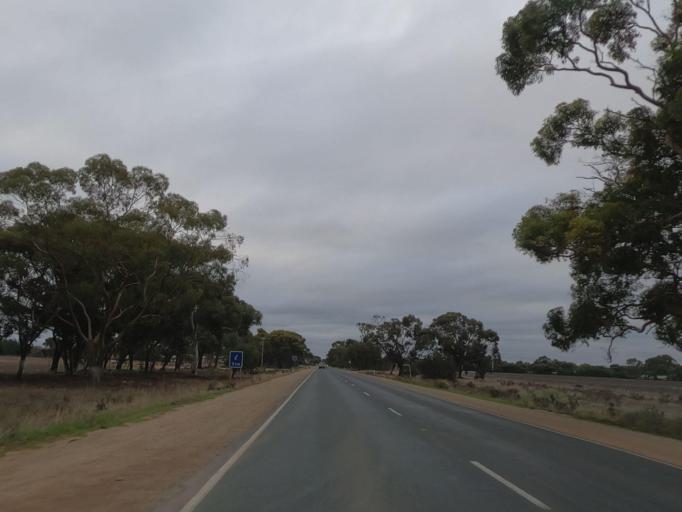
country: AU
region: Victoria
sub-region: Swan Hill
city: Swan Hill
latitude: -35.3711
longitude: 143.5622
